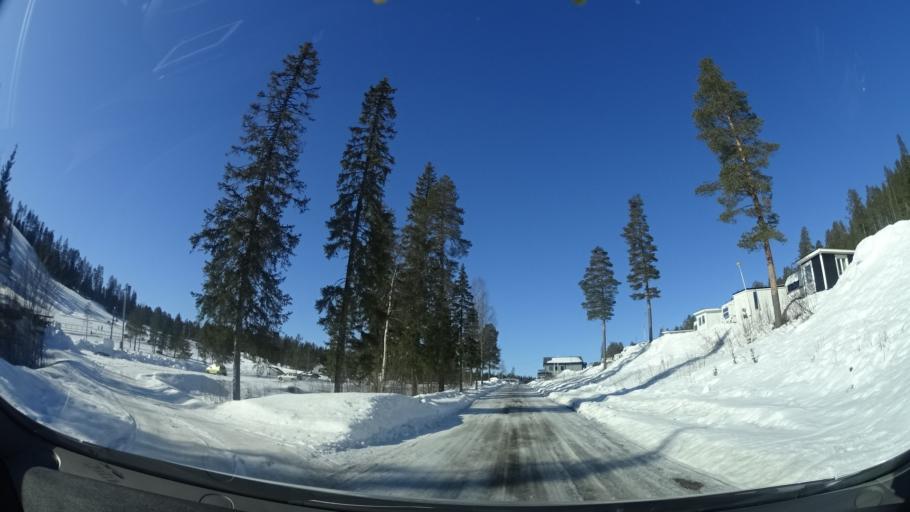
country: SE
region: Vaesterbotten
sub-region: Skelleftea Kommun
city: Langsele
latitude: 65.1631
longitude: 20.1365
